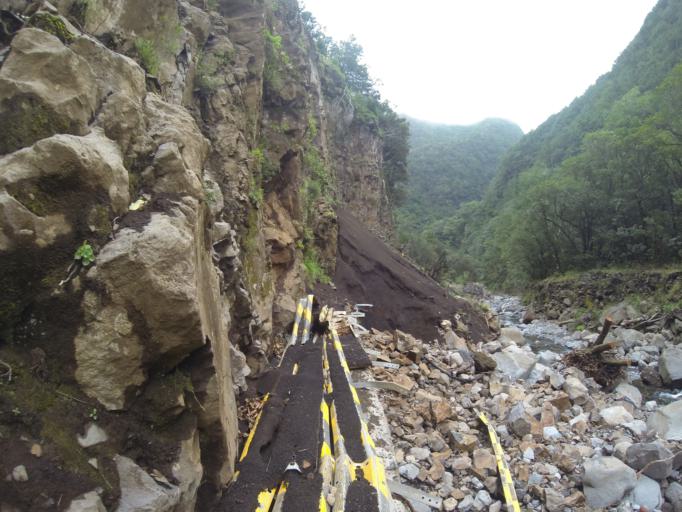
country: PT
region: Madeira
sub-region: Sao Vicente
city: Sao Vicente
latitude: 32.7915
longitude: -17.1139
